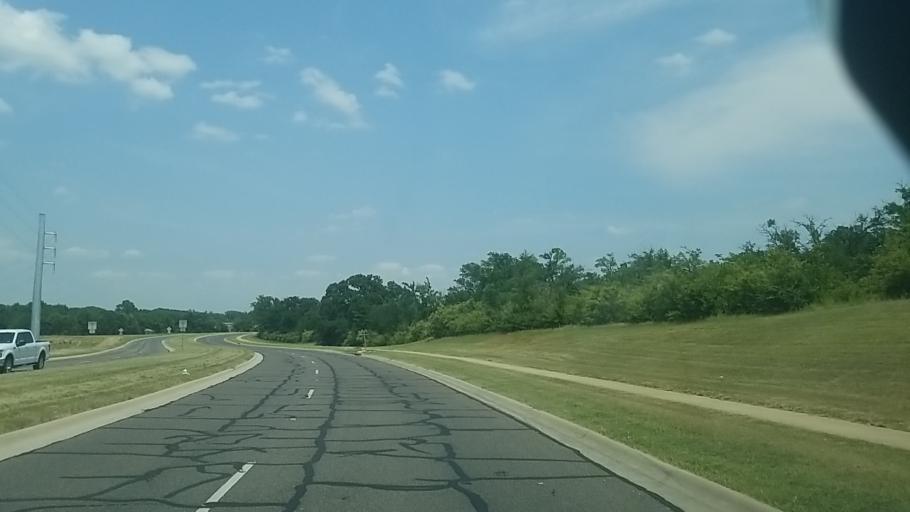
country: US
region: Texas
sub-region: Denton County
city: Denton
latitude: 33.2037
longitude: -97.0953
